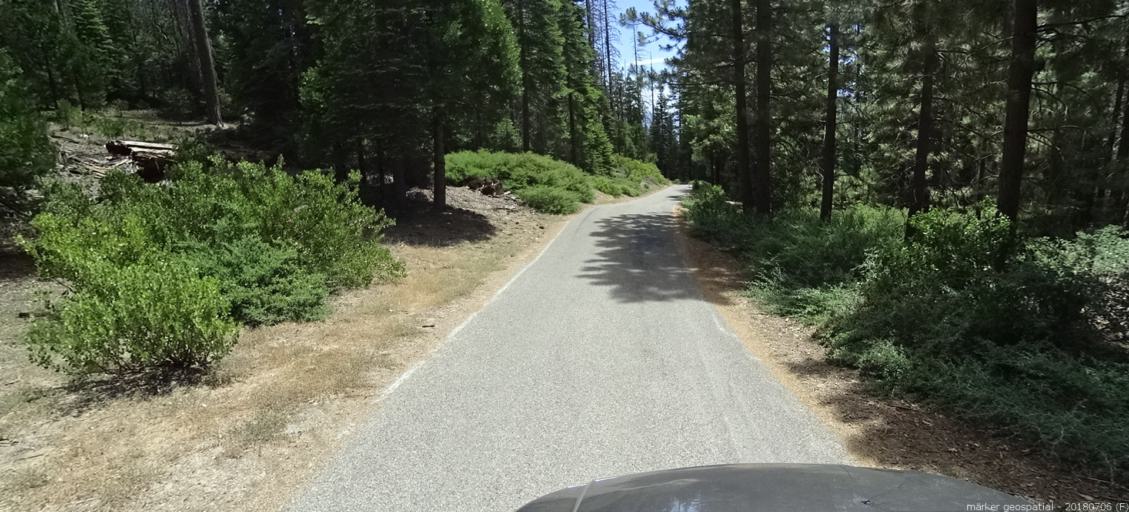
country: US
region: California
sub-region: Madera County
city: Oakhurst
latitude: 37.4077
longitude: -119.4096
